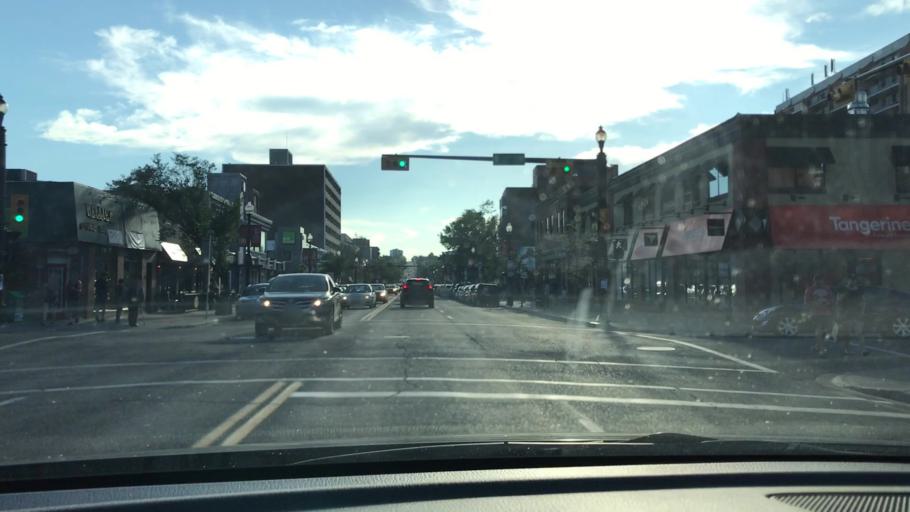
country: CA
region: Alberta
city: Calgary
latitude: 51.0378
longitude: -114.0840
